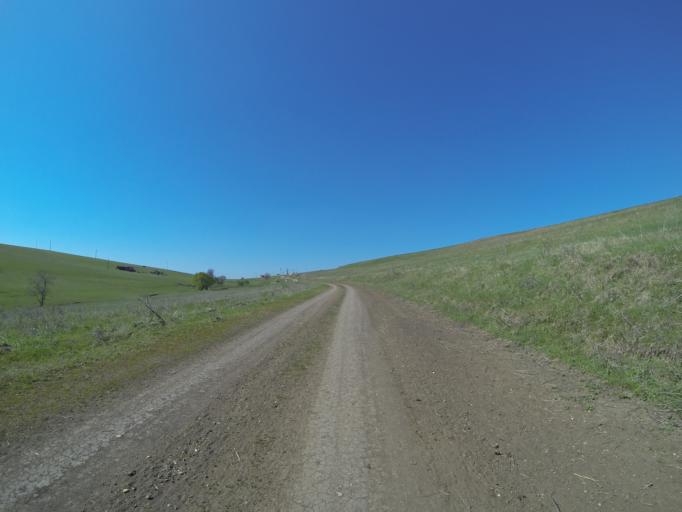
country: RO
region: Dolj
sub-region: Comuna Caloparu
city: Salcuta
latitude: 44.1572
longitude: 23.6709
